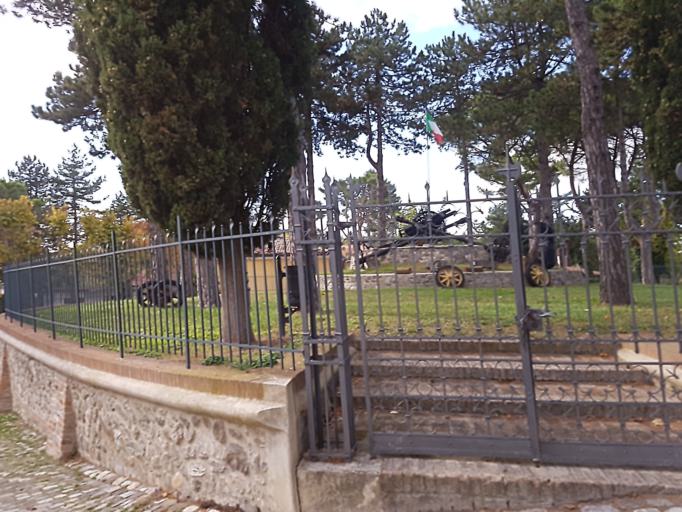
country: IT
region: Emilia-Romagna
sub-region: Provincia di Rimini
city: Monte Colombo
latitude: 43.9206
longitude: 12.5524
